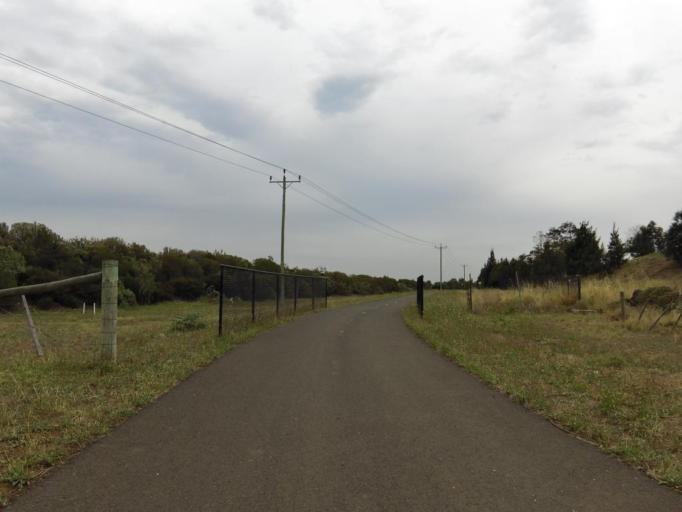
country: AU
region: Victoria
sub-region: Brimbank
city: Derrimut
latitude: -37.7977
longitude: 144.7716
